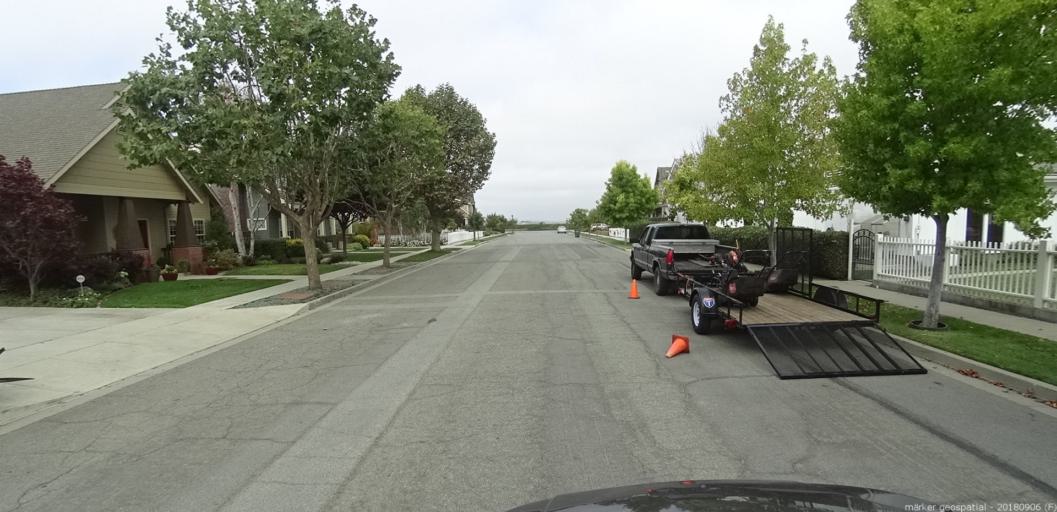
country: US
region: California
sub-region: Monterey County
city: Salinas
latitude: 36.6256
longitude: -121.6480
